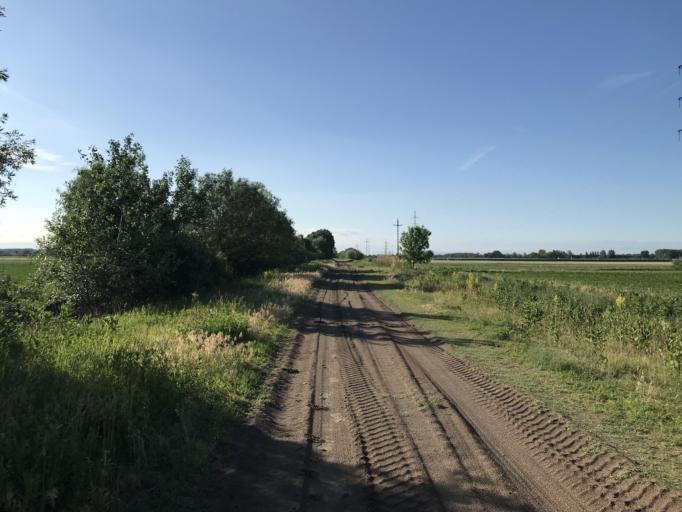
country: HU
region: Bacs-Kiskun
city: Tiszakecske
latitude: 46.9627
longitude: 20.0760
